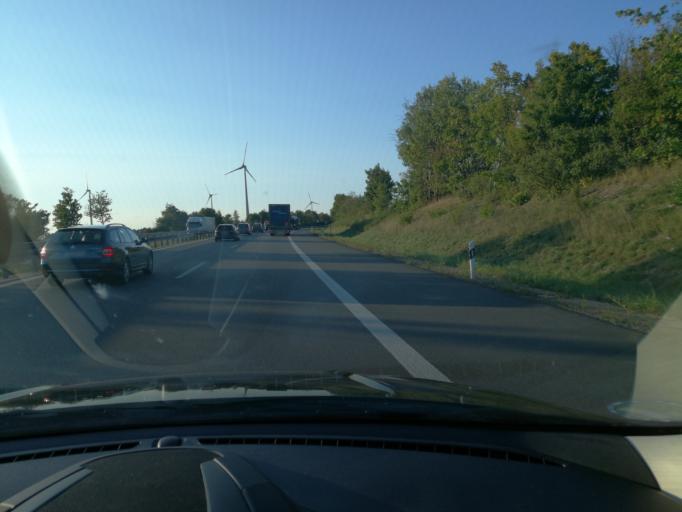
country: DE
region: Bavaria
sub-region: Upper Palatinate
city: Pilsach
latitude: 49.2959
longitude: 11.5543
